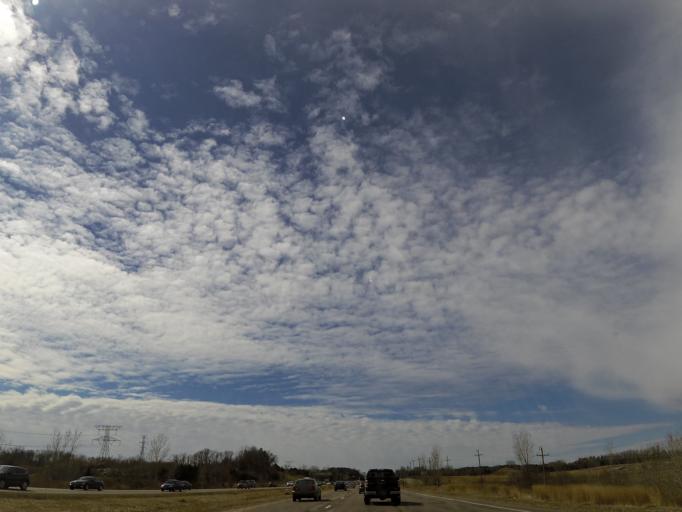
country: US
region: Minnesota
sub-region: Washington County
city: Lake Elmo
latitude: 45.0362
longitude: -92.8536
